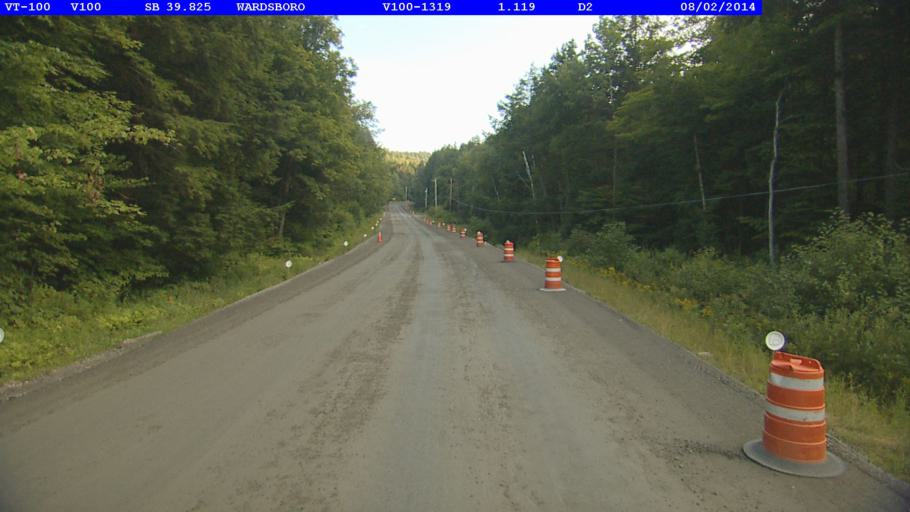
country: US
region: Vermont
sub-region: Windham County
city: Dover
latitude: 43.0157
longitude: -72.8610
